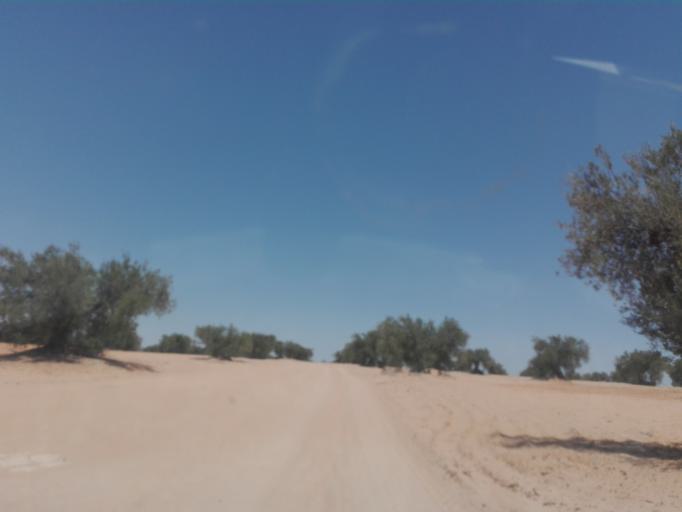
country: TN
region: Safaqis
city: Bi'r `Ali Bin Khalifah
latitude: 34.6493
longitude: 10.2737
